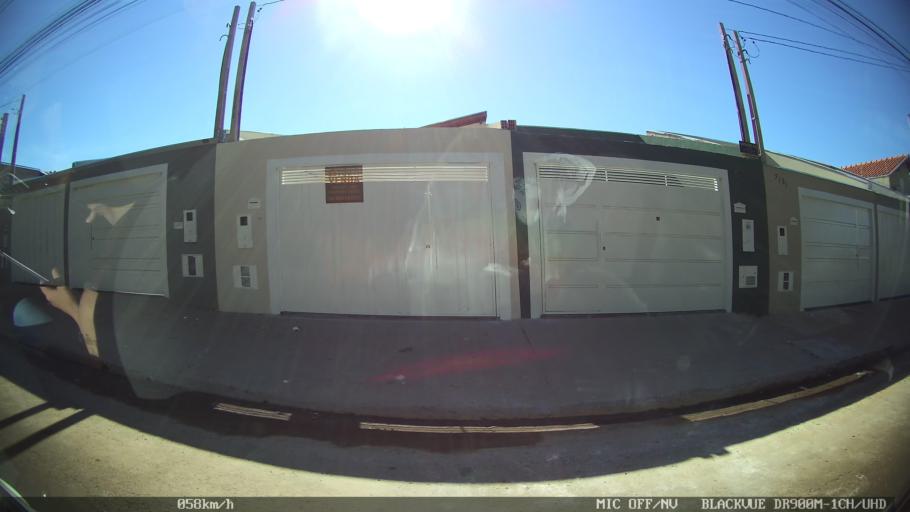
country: BR
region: Sao Paulo
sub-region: Franca
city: Franca
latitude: -20.5663
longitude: -47.3540
